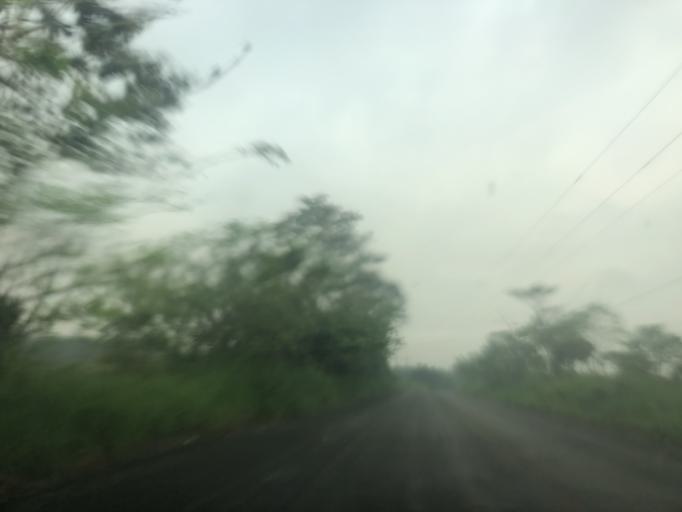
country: MX
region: Chiapas
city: Pueblo Juarez
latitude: 17.6292
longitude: -93.1642
